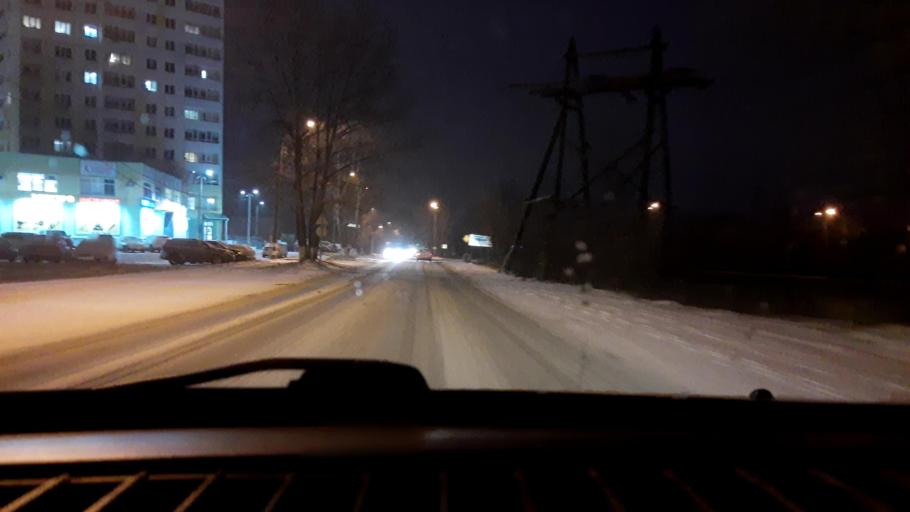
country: RU
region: Nizjnij Novgorod
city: Bor
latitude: 56.3336
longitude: 44.1067
